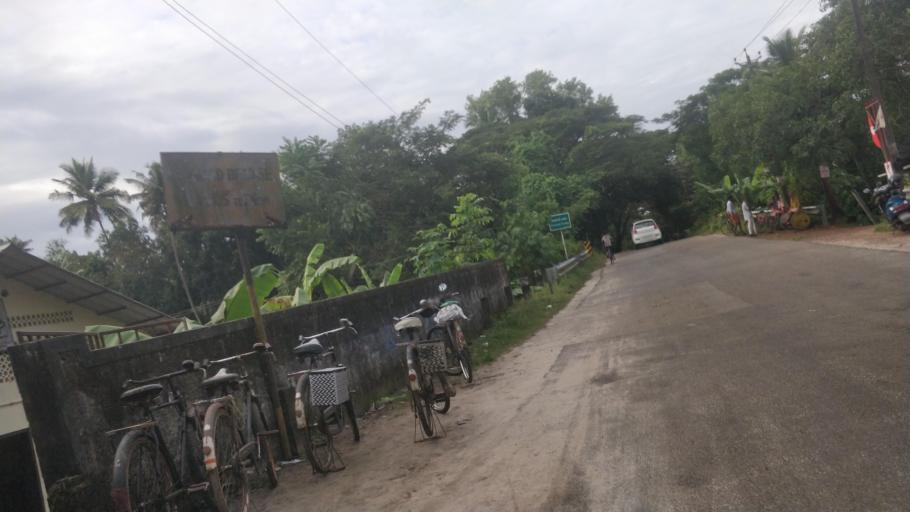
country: IN
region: Kerala
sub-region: Alappuzha
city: Shertallai
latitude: 9.6912
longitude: 76.3606
